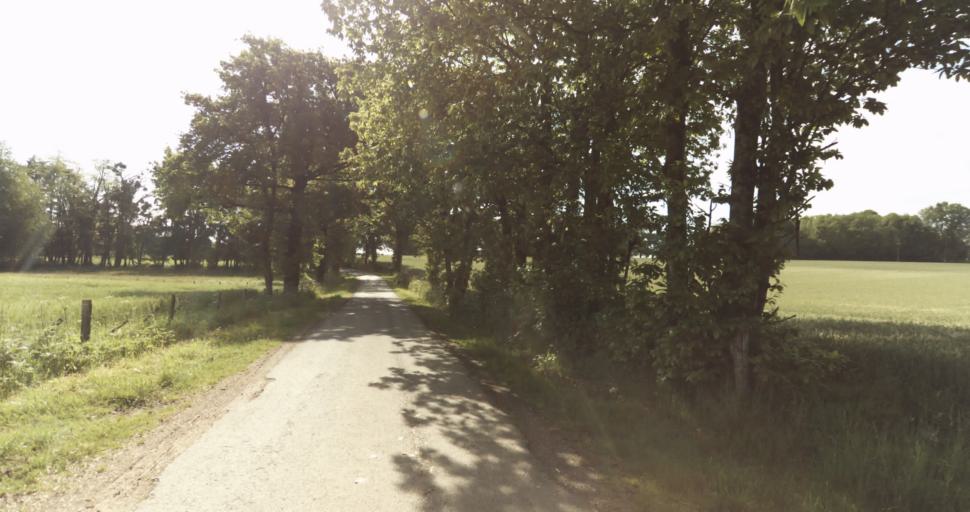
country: FR
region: Limousin
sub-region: Departement de la Haute-Vienne
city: Solignac
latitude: 45.7197
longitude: 1.2650
